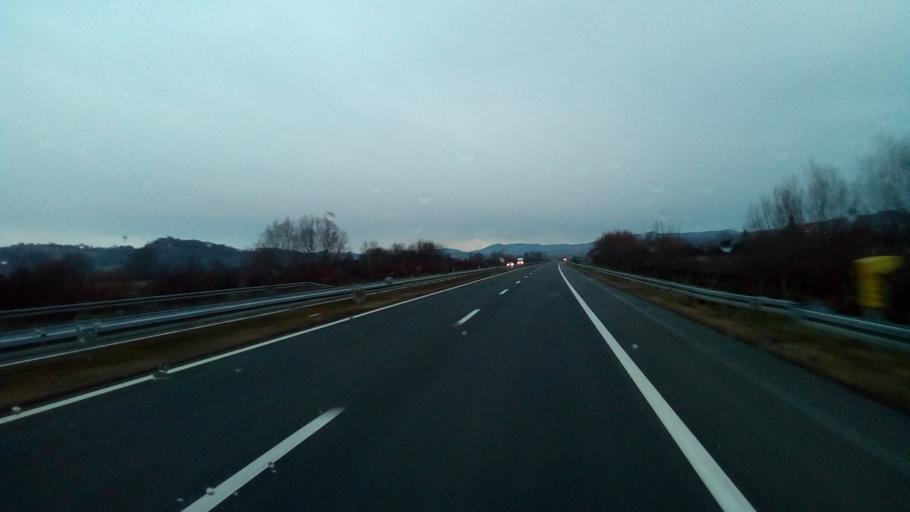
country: HR
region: Varazdinska
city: Remetinec
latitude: 46.0257
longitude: 16.2948
